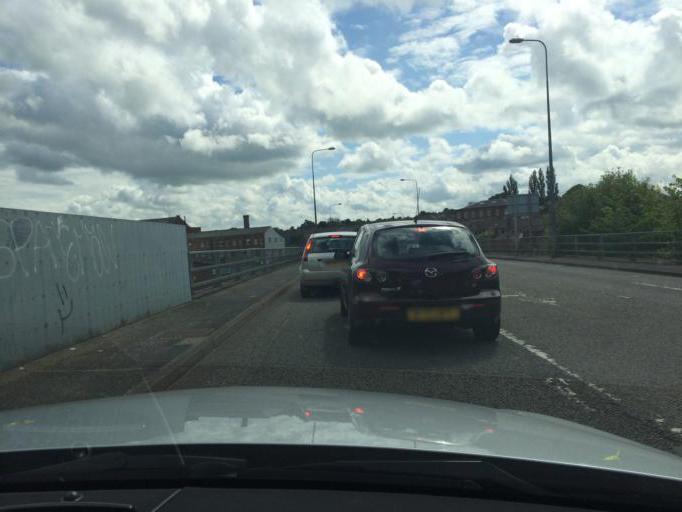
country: GB
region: England
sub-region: Cheshire East
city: Macclesfield
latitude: 53.2559
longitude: -2.1204
